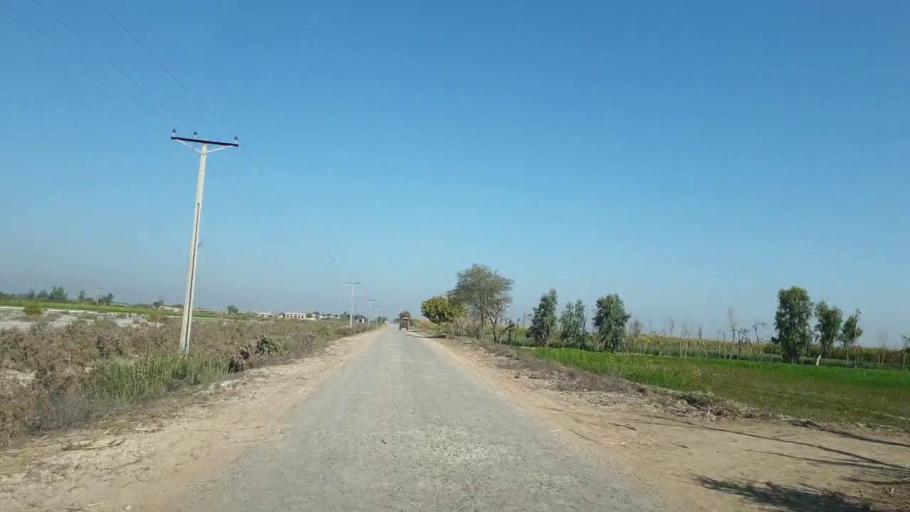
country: PK
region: Sindh
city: Mirpur Khas
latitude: 25.5922
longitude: 69.0454
